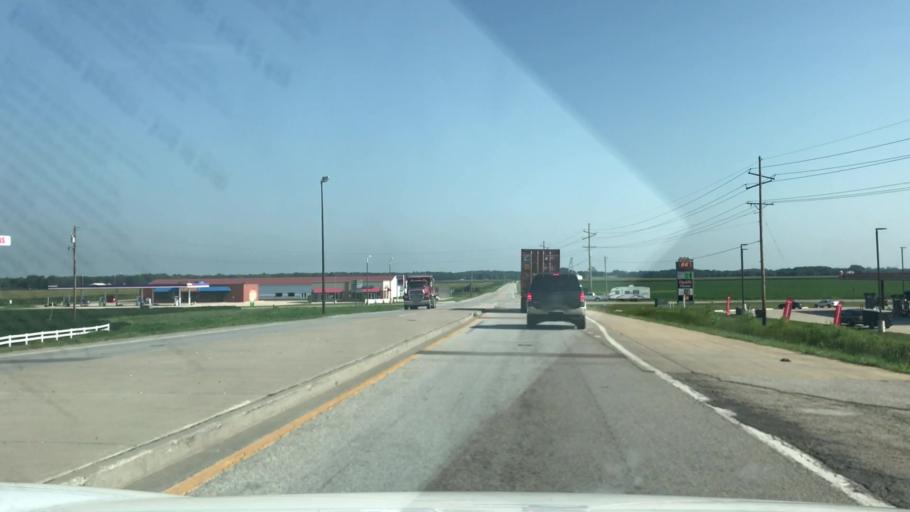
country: US
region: Illinois
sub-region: Saint Clair County
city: Scott Air Force Base
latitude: 38.5545
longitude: -89.8071
